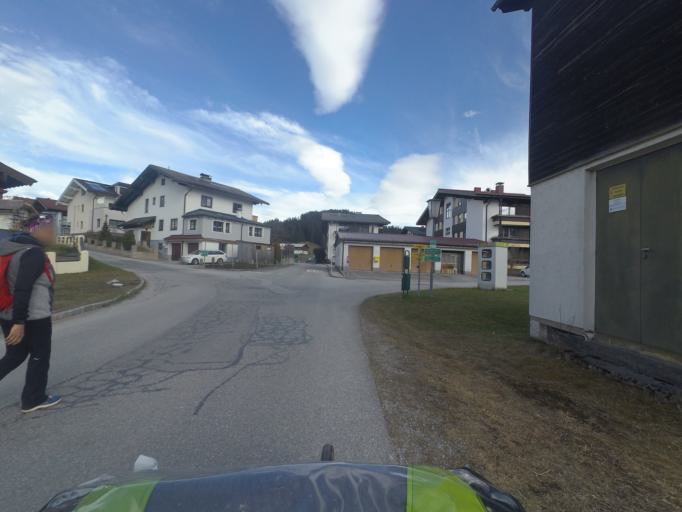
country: AT
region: Salzburg
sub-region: Politischer Bezirk Hallein
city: Abtenau
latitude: 47.5738
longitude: 13.3464
